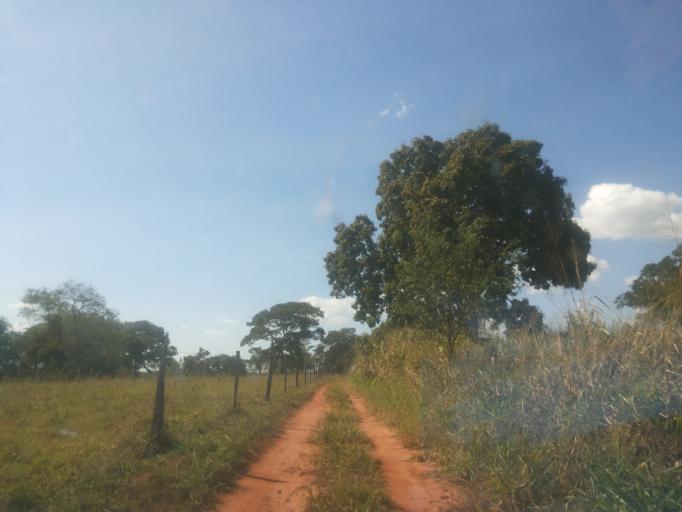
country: BR
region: Minas Gerais
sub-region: Santa Vitoria
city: Santa Vitoria
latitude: -18.9954
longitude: -50.3766
